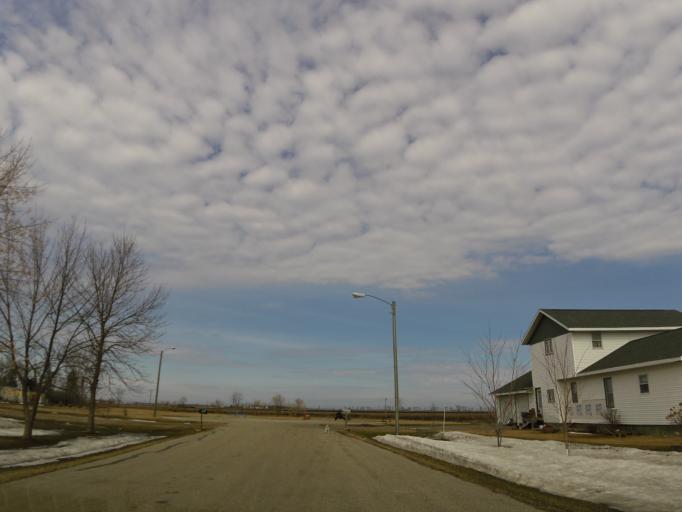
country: US
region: North Dakota
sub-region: Walsh County
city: Grafton
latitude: 48.2945
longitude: -97.3785
